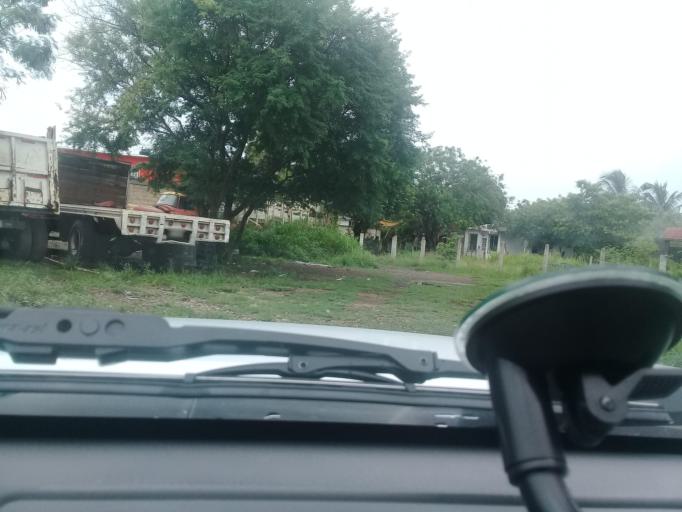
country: MX
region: Veracruz
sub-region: Puente Nacional
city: Cabezas
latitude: 19.3688
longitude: -96.3856
